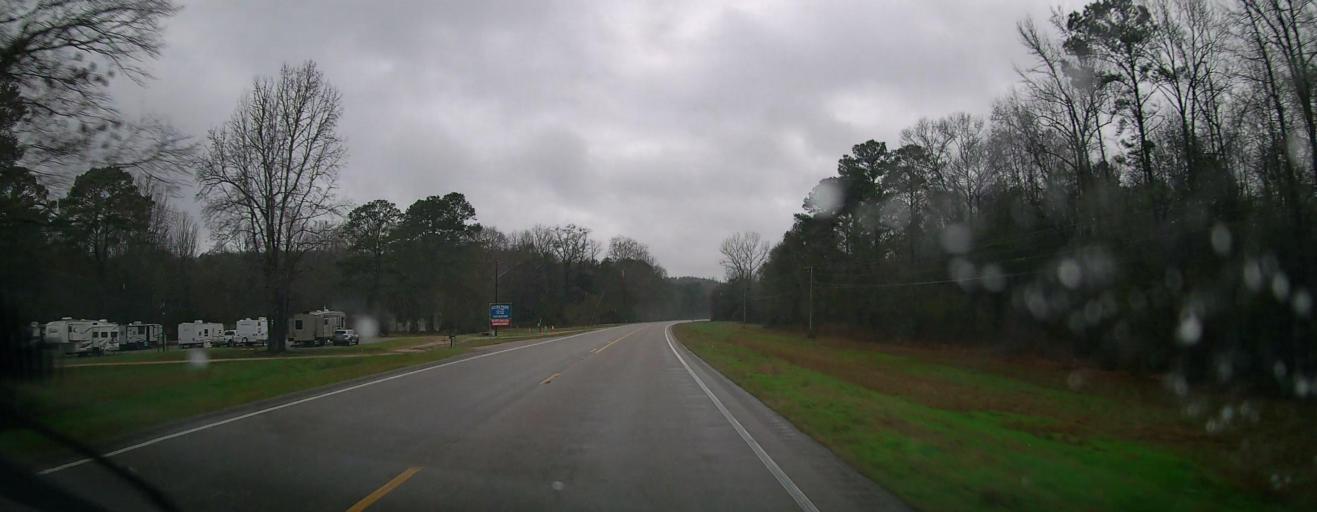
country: US
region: Alabama
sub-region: Autauga County
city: Prattville
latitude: 32.4903
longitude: -86.5659
